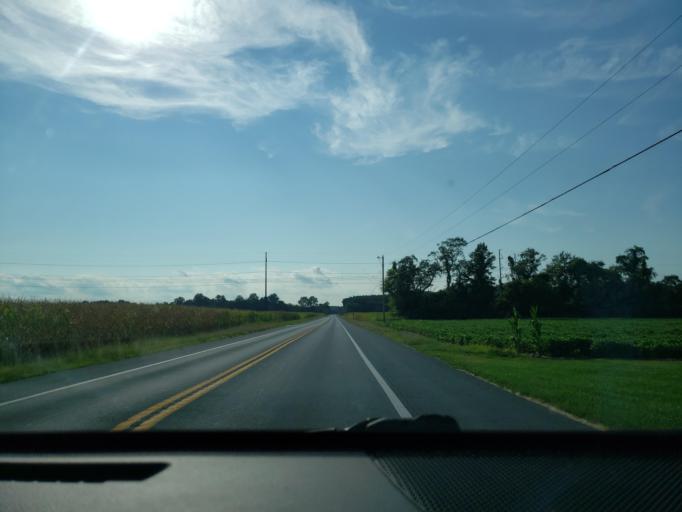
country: US
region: Delaware
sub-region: Sussex County
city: Milton
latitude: 38.7642
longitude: -75.2735
